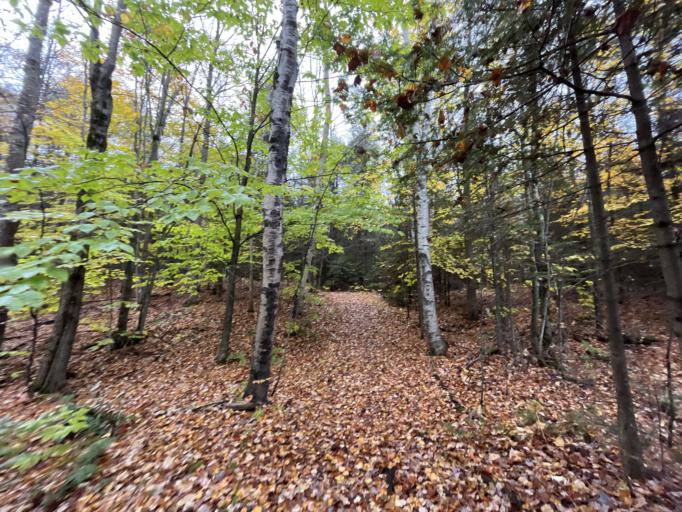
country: US
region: New Hampshire
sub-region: Merrimack County
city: New London
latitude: 43.3972
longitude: -71.9990
